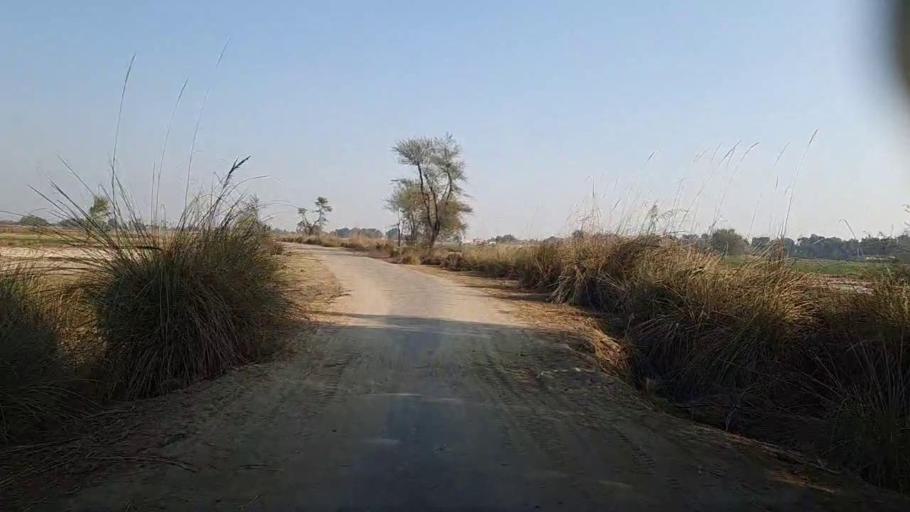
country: PK
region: Sindh
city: Mirpur Mathelo
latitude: 27.8747
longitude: 69.6268
